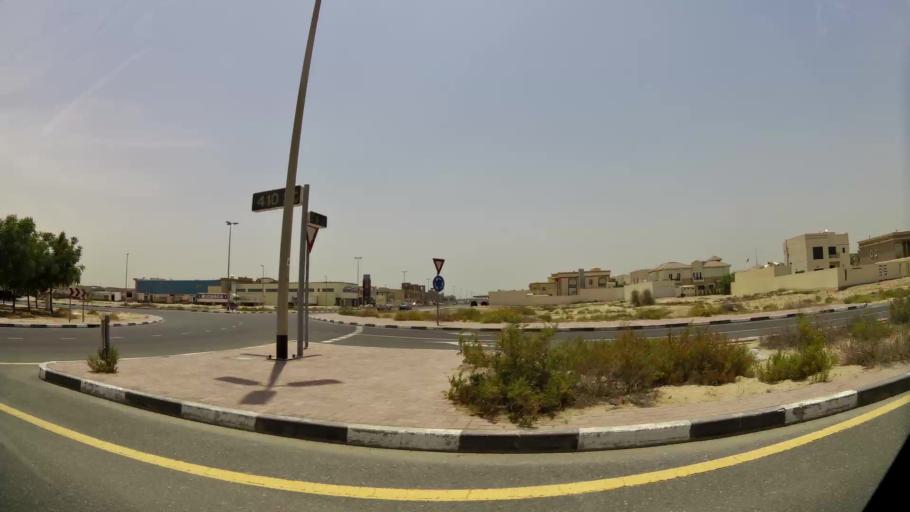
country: AE
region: Ash Shariqah
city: Sharjah
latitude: 25.1890
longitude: 55.3873
